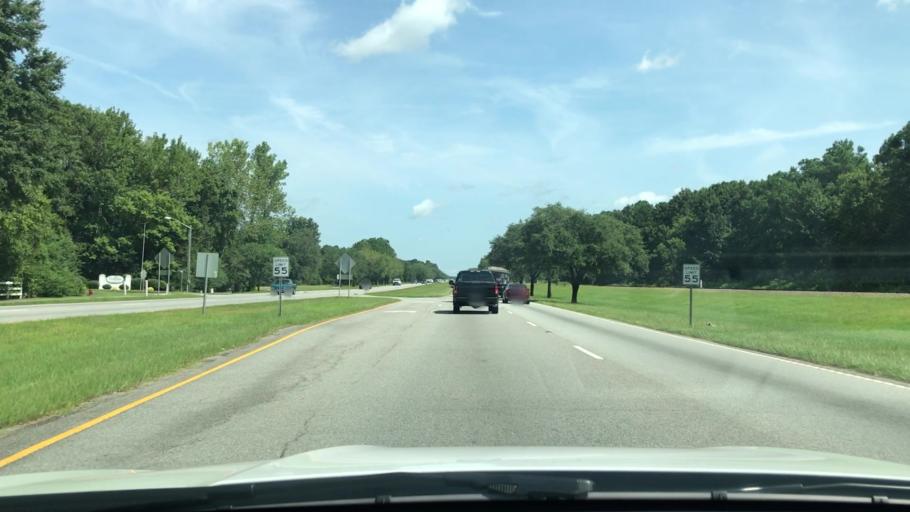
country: US
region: South Carolina
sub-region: Berkeley County
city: Goose Creek
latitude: 33.0201
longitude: -80.0357
